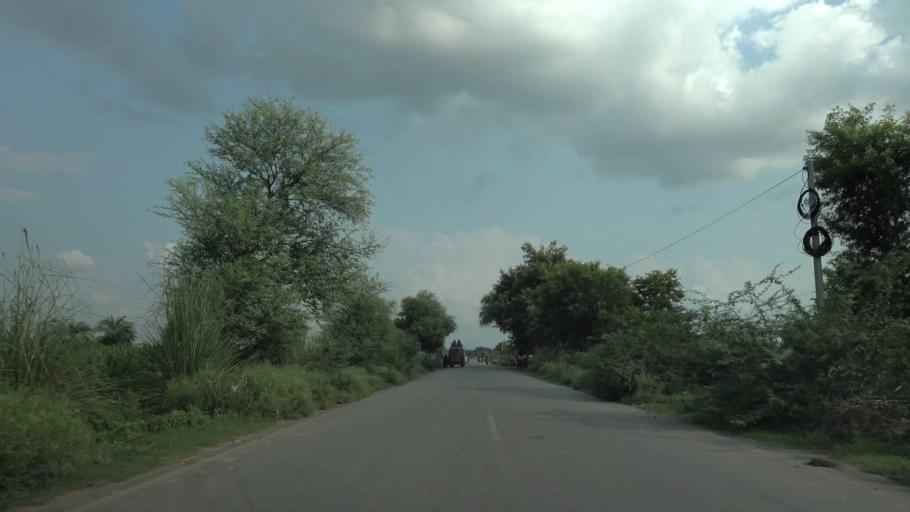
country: PK
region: Punjab
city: Nankana Sahib
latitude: 31.4888
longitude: 73.6072
